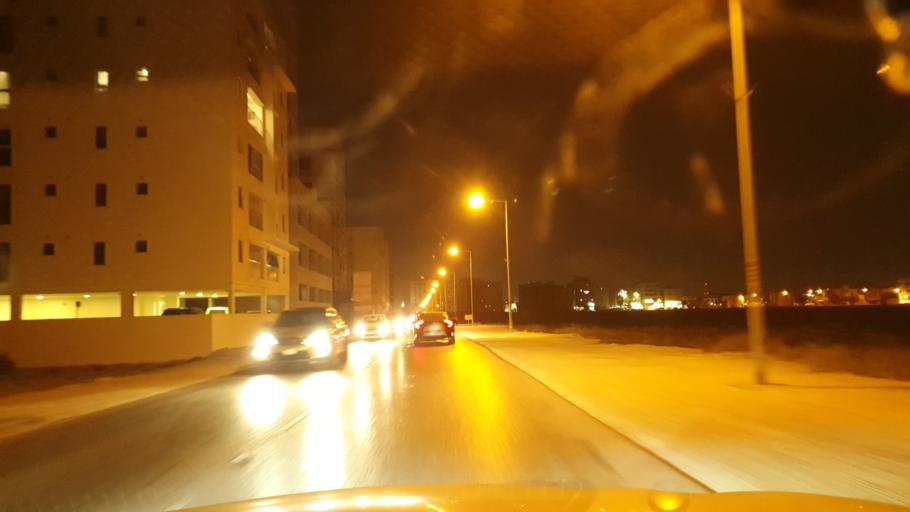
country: BH
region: Northern
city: Madinat `Isa
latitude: 26.1852
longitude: 50.4820
